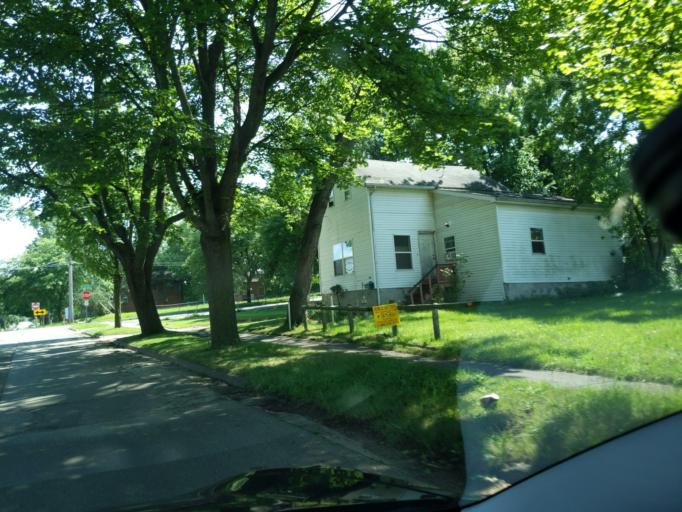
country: US
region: Michigan
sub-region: Jackson County
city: Jackson
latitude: 42.2553
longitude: -84.4119
